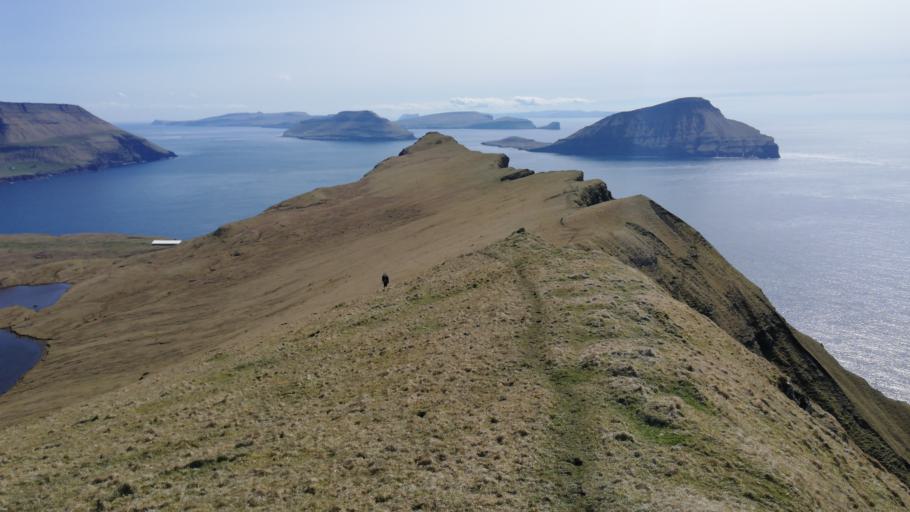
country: FO
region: Streymoy
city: Kollafjordhur
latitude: 62.0512
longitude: -6.9869
